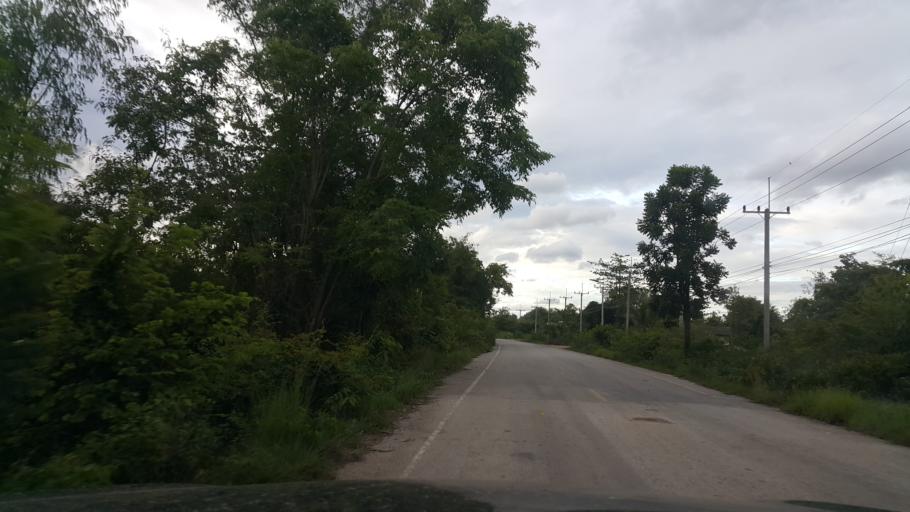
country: TH
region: Sukhothai
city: Thung Saliam
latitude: 17.1760
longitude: 99.5250
